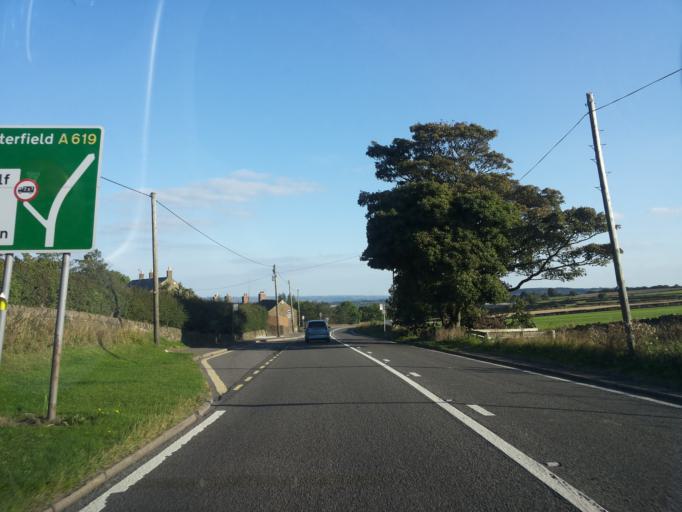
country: GB
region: England
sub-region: Derbyshire
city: Dronfield
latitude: 53.2354
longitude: -1.5340
